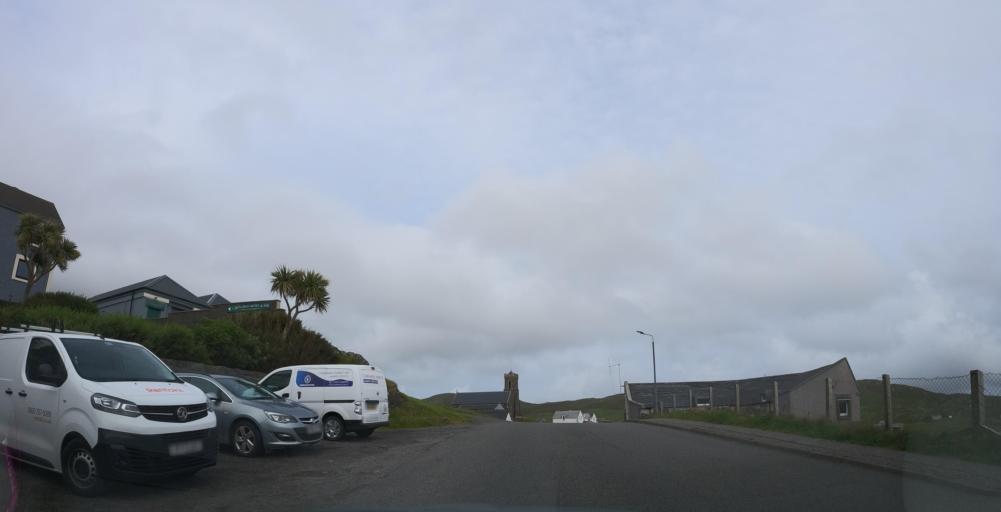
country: GB
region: Scotland
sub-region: Eilean Siar
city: Barra
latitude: 56.9552
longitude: -7.4875
